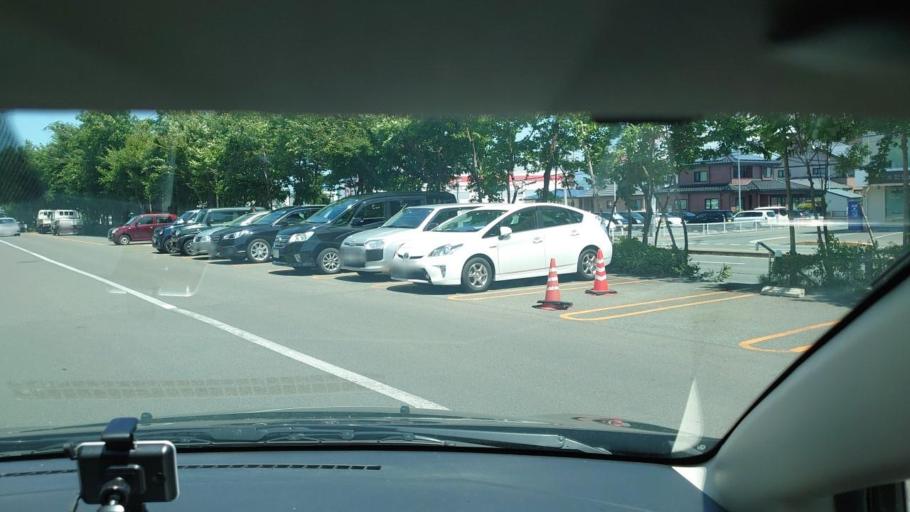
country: JP
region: Iwate
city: Morioka-shi
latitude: 39.6837
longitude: 141.1297
